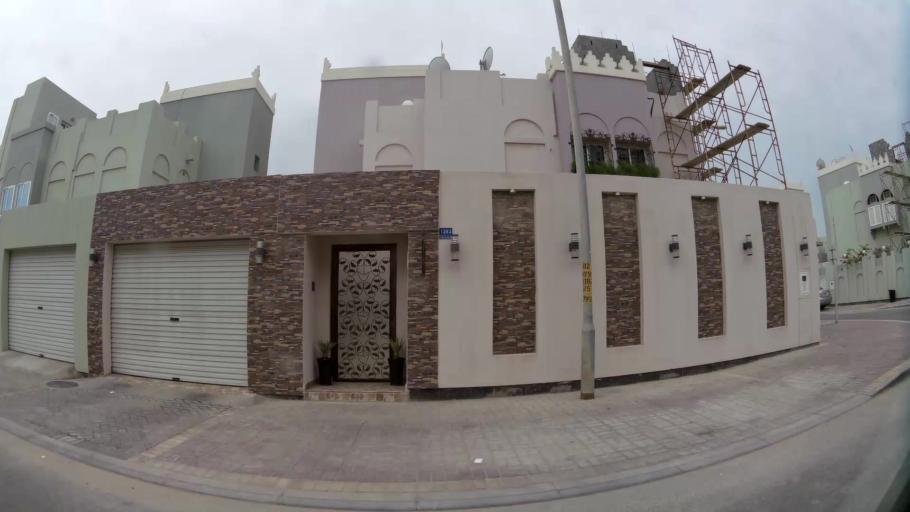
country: BH
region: Northern
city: Madinat `Isa
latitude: 26.1655
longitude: 50.5408
